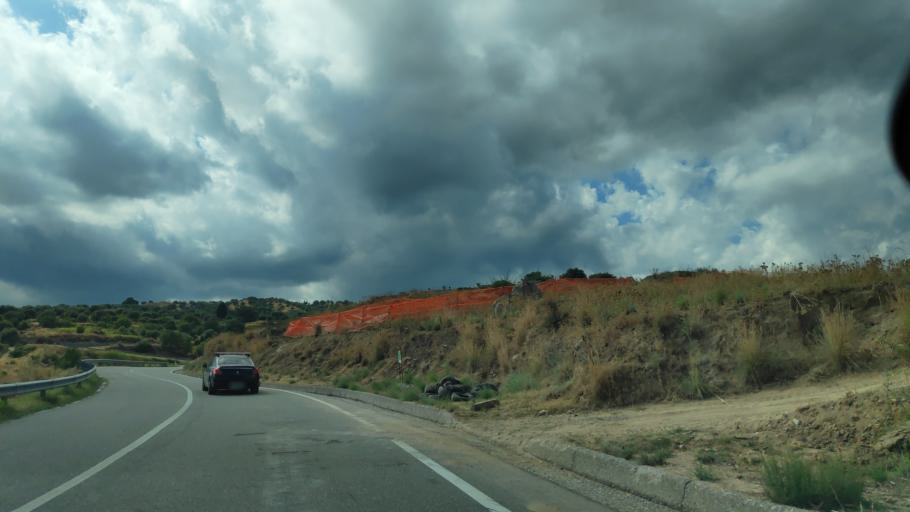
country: IT
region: Calabria
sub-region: Provincia di Catanzaro
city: Santa Caterina dello Ionio
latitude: 38.5239
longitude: 16.5367
